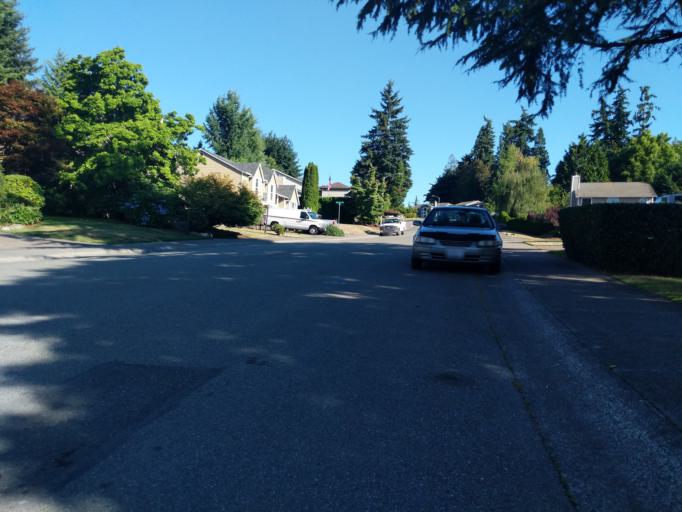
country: US
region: Washington
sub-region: King County
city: Bothell
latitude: 47.7854
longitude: -122.2050
